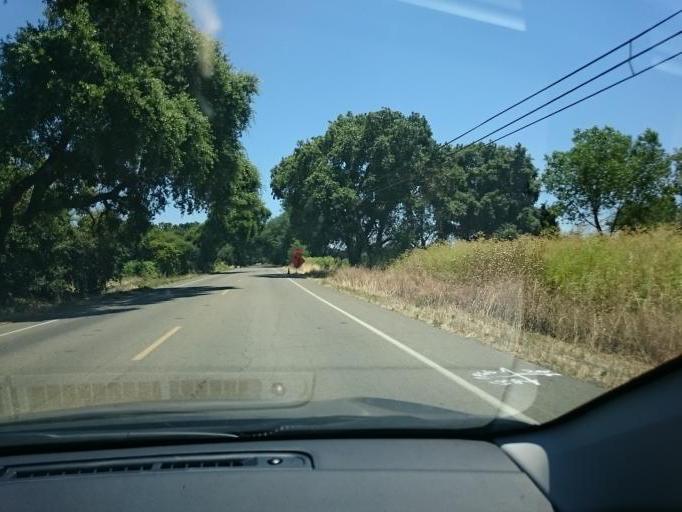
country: US
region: California
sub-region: San Joaquin County
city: Thornton
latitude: 38.2254
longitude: -121.4541
